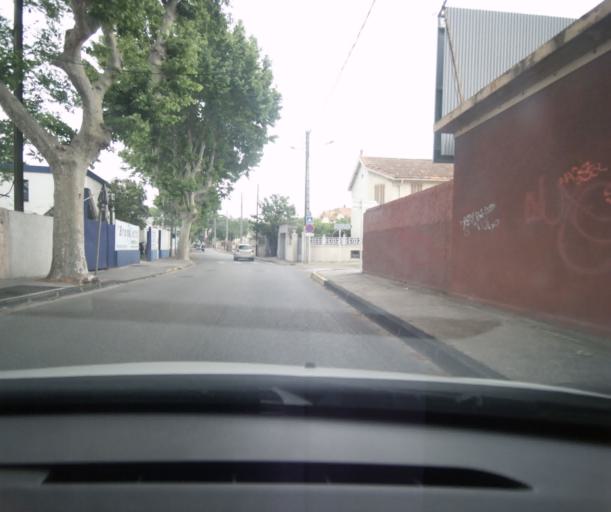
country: FR
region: Provence-Alpes-Cote d'Azur
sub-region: Departement du Var
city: Toulon
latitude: 43.1201
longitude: 5.9533
